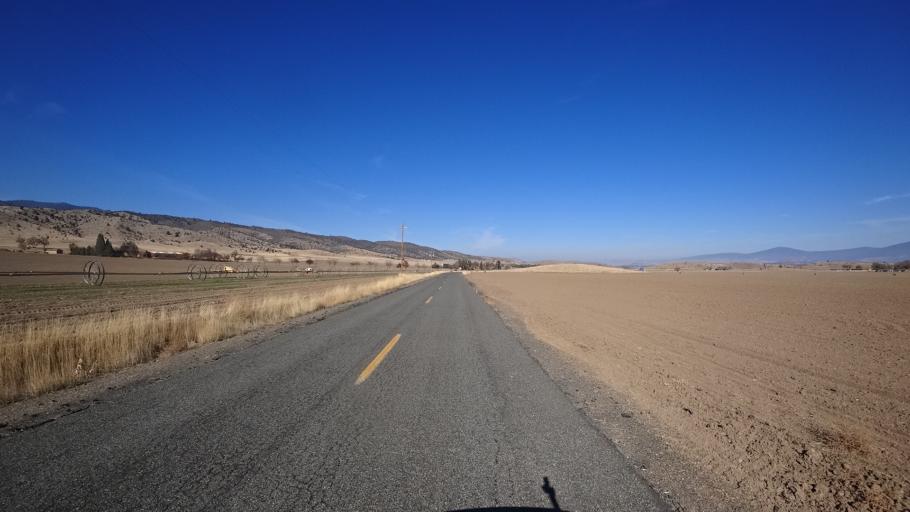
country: US
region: California
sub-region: Siskiyou County
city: Montague
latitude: 41.5698
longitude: -122.5490
